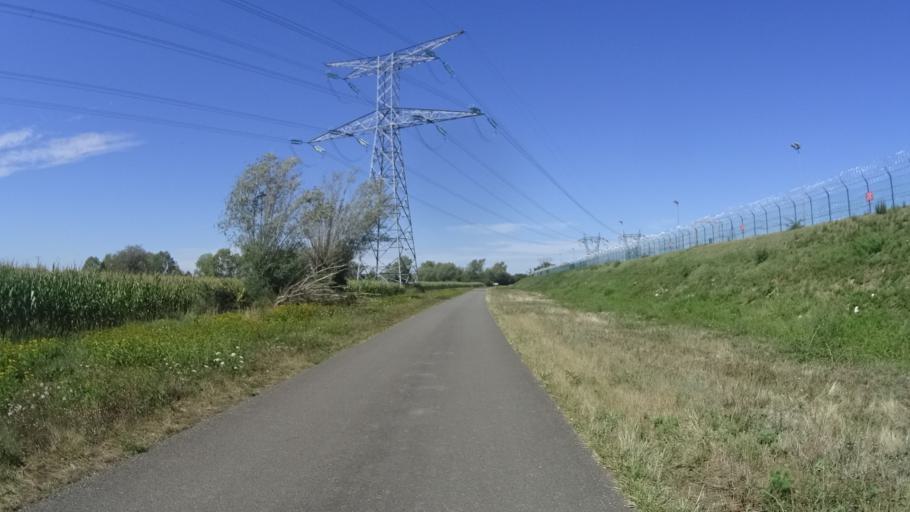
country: FR
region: Bourgogne
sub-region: Departement de la Nievre
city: Neuvy-sur-Loire
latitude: 47.5033
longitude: 2.8757
